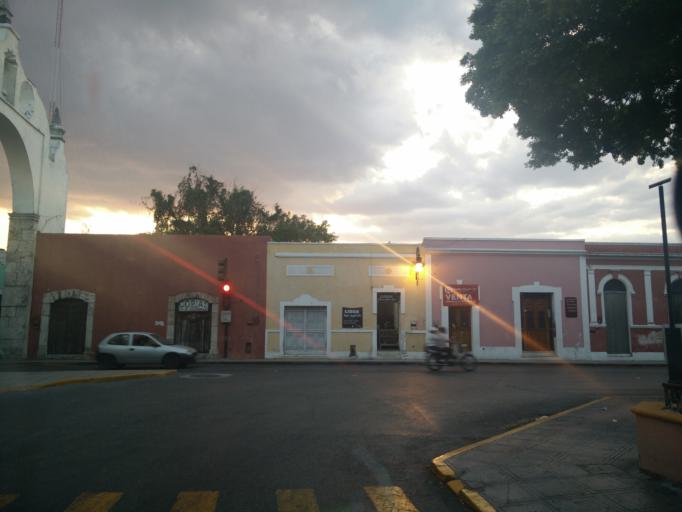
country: MX
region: Yucatan
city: Merida
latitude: 20.9623
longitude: -89.6267
